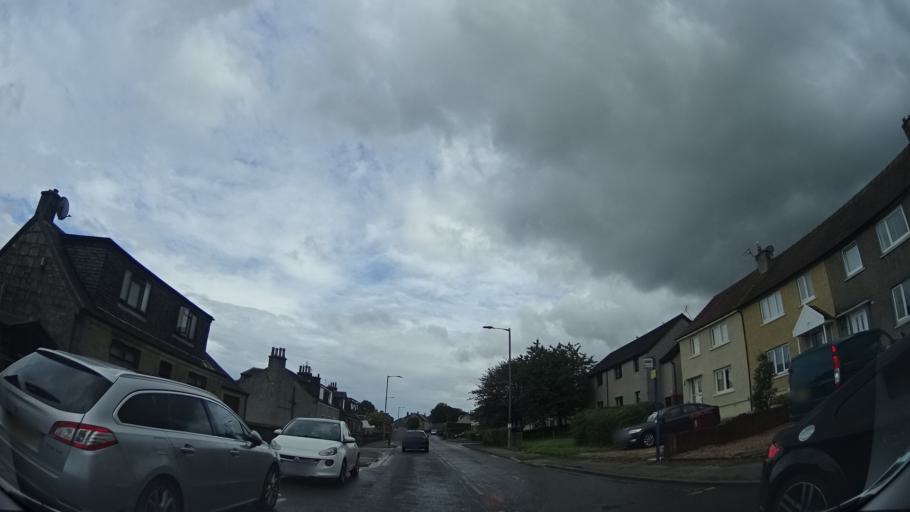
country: GB
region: Scotland
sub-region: Falkirk
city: Bonnybridge
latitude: 56.0023
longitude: -3.8837
